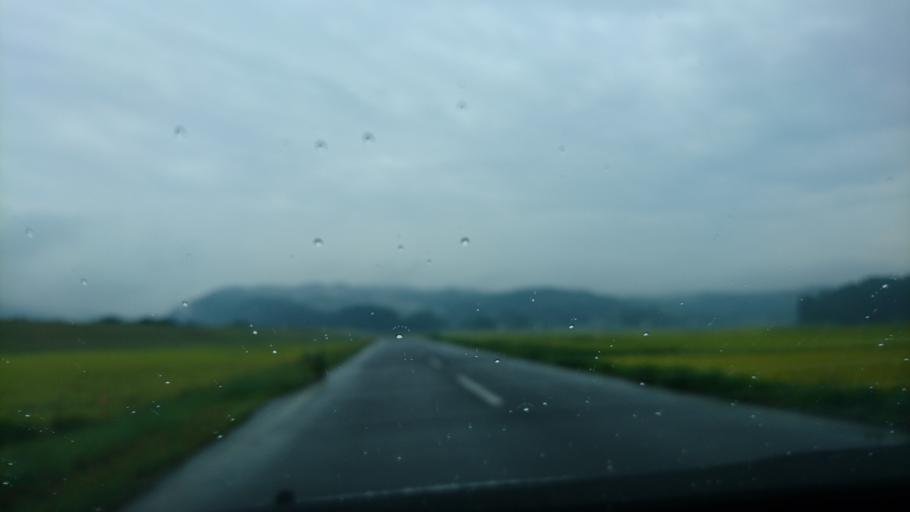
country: JP
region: Iwate
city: Ichinoseki
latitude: 38.8876
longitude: 141.2599
